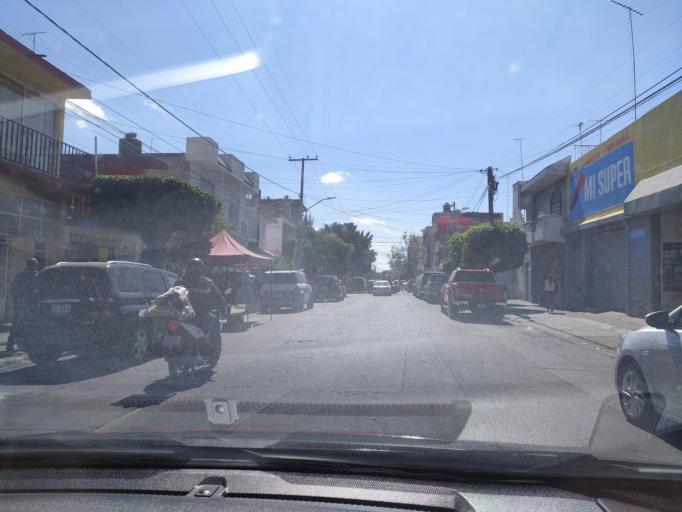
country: LA
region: Oudomxai
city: Muang La
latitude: 21.0140
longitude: 101.8566
